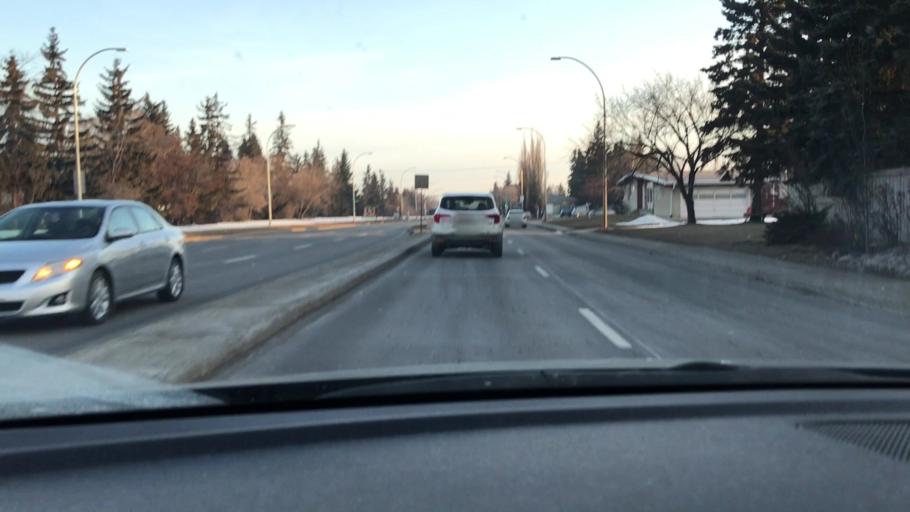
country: CA
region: Alberta
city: Edmonton
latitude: 53.5191
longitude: -113.4429
